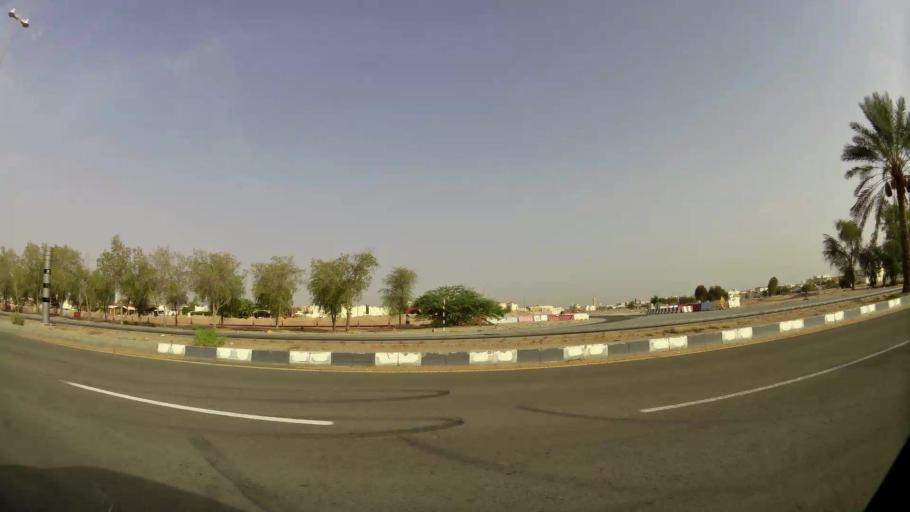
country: AE
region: Abu Dhabi
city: Al Ain
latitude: 24.1119
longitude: 55.6998
